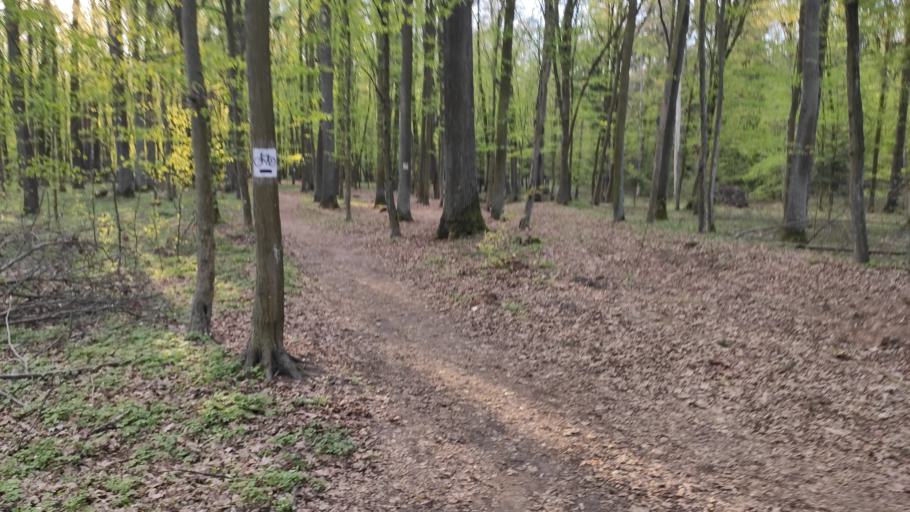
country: PL
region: Masovian Voivodeship
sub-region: Powiat radomski
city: Pionki
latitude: 51.4748
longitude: 21.4370
